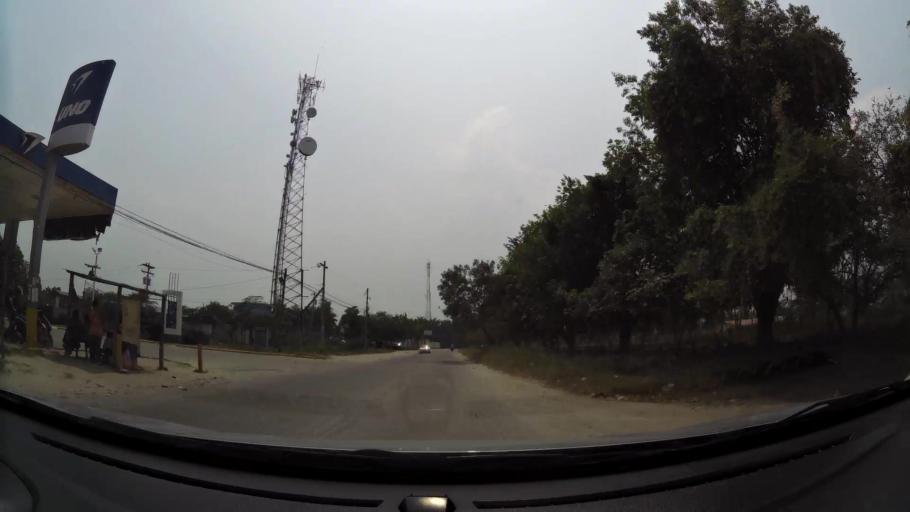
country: HN
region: Cortes
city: La Lima
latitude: 15.4363
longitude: -87.9126
